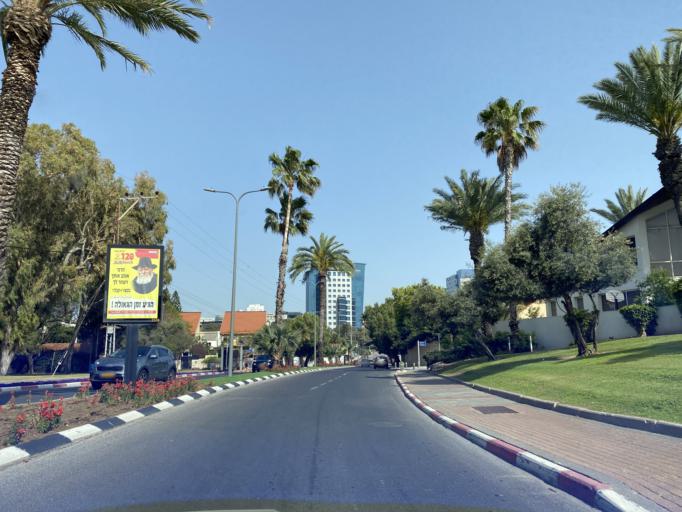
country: IL
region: Tel Aviv
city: Herzliya Pituah
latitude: 32.1677
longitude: 34.8061
